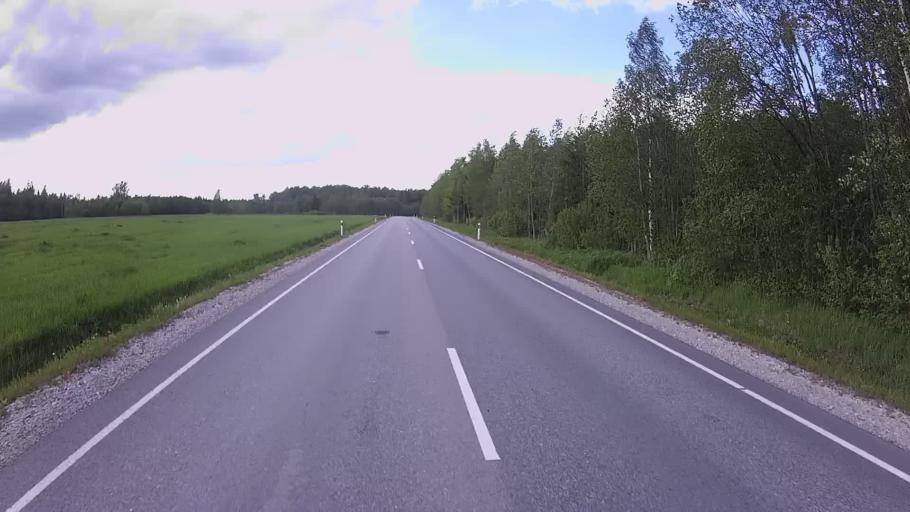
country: EE
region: Jogevamaa
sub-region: Mustvee linn
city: Mustvee
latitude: 58.8771
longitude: 26.8188
